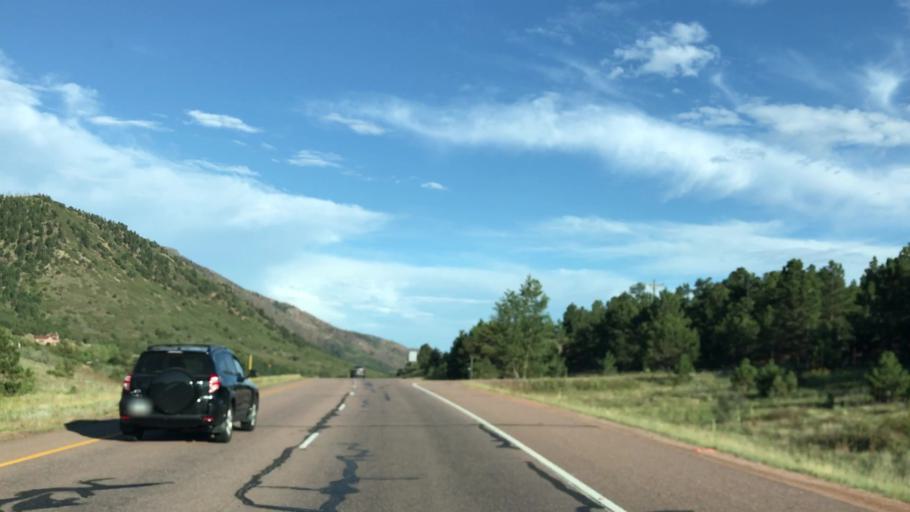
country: US
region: Colorado
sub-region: El Paso County
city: Cascade-Chipita Park
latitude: 38.9346
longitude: -105.0074
